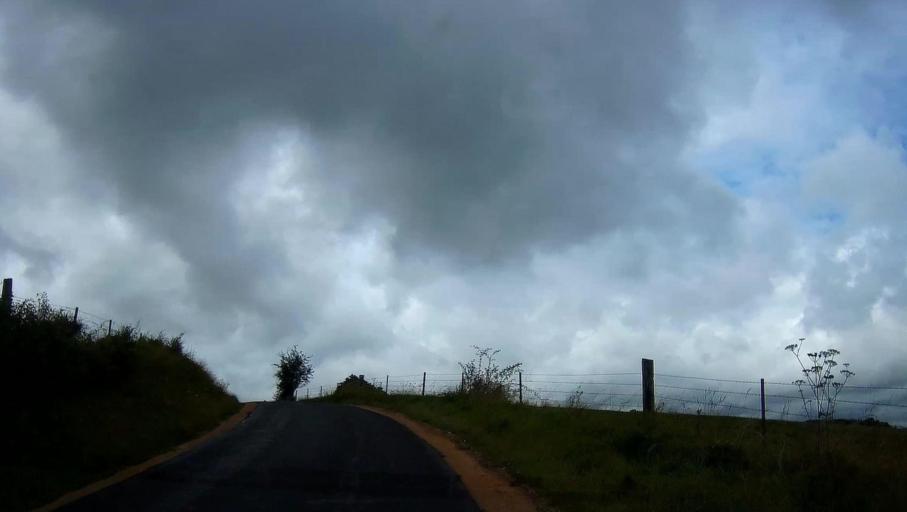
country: FR
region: Champagne-Ardenne
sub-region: Departement des Ardennes
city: Rimogne
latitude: 49.7601
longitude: 4.5176
